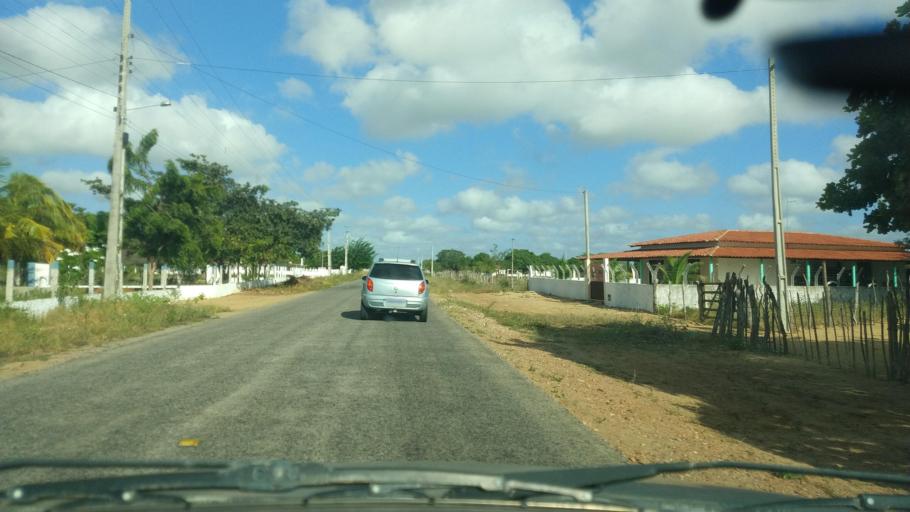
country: BR
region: Rio Grande do Norte
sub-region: Sao Paulo Do Potengi
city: Sao Paulo do Potengi
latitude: -5.9159
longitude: -35.7173
